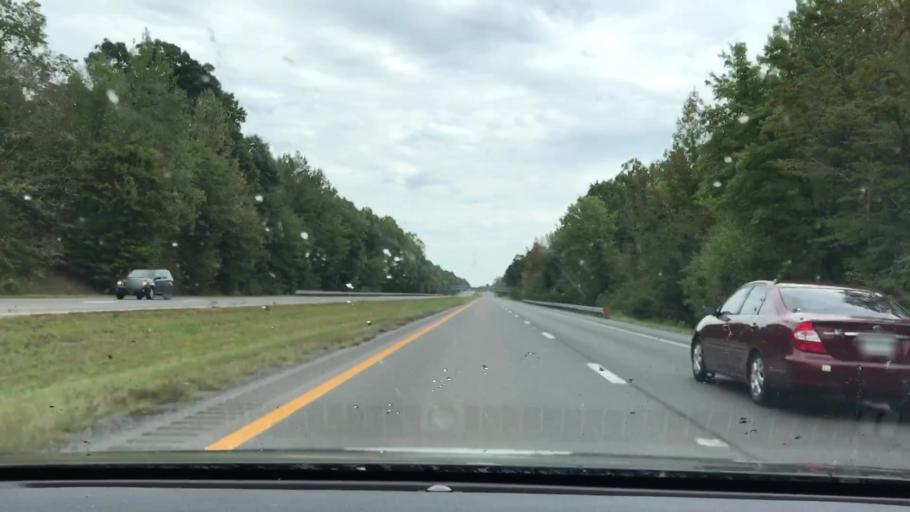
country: US
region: Kentucky
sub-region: Marshall County
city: Benton
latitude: 36.8342
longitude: -88.4366
